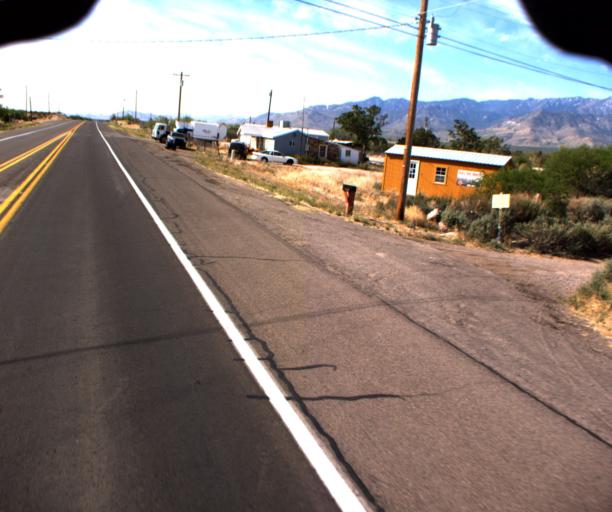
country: US
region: Arizona
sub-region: Graham County
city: Cactus Flat
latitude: 32.7578
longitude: -109.7163
